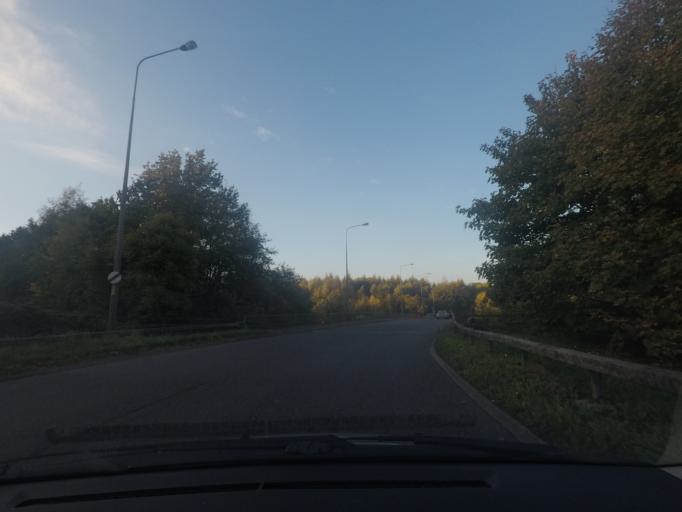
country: GB
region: England
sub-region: North Lincolnshire
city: Scawby
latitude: 53.5440
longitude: -0.5588
